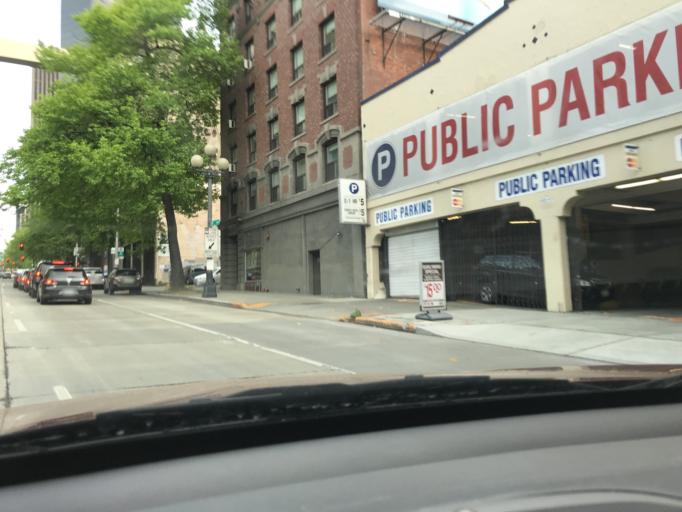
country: US
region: Washington
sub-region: King County
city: Seattle
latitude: 47.6019
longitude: -122.3291
